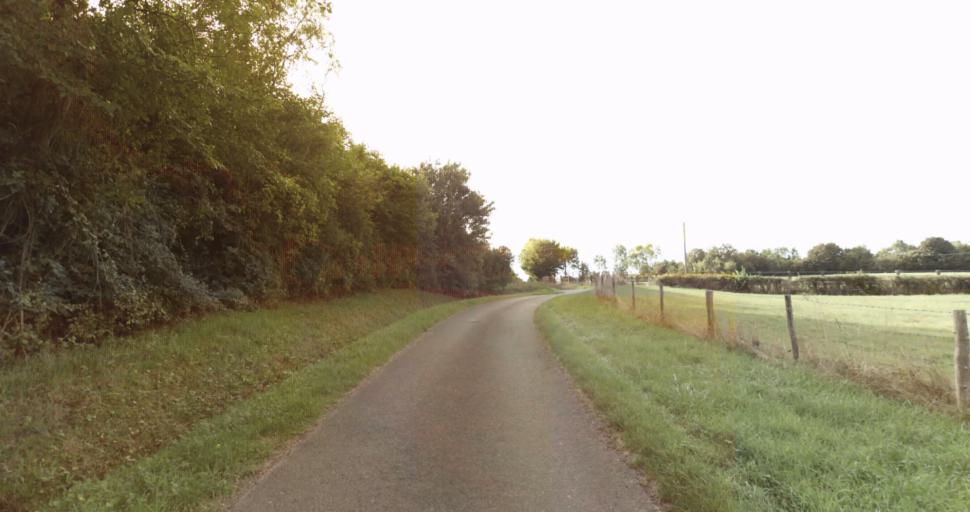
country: FR
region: Lower Normandy
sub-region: Departement de l'Orne
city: Gace
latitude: 48.7026
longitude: 0.2953
